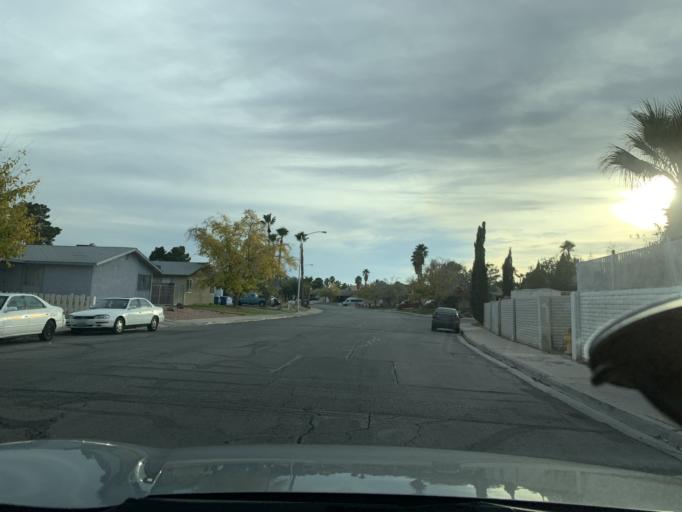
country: US
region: Nevada
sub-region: Clark County
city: Spring Valley
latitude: 36.0984
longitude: -115.2310
